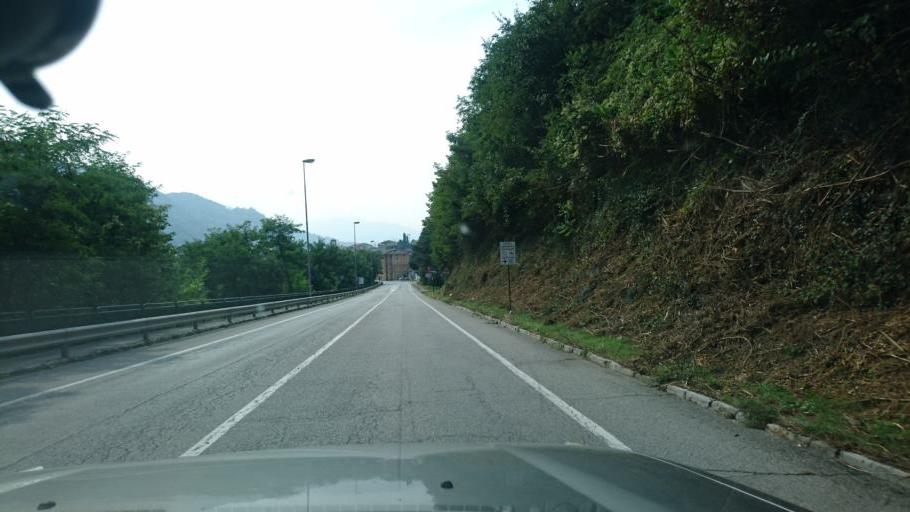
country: IT
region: Lombardy
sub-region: Provincia di Brescia
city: Vestone
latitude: 45.7128
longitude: 10.4102
